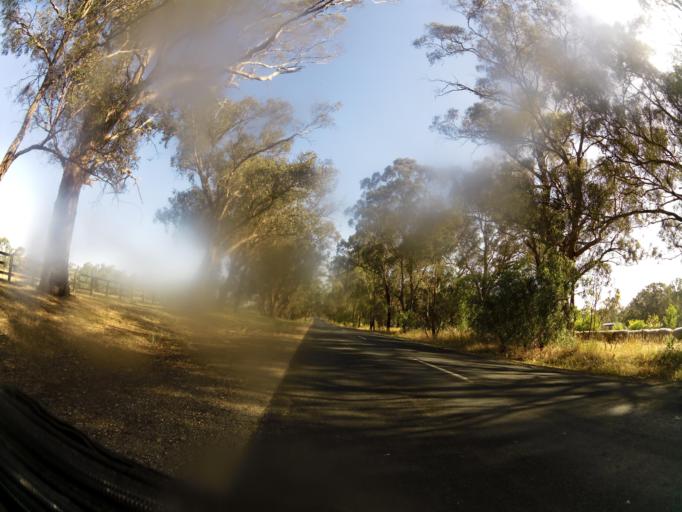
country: AU
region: Victoria
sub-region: Murrindindi
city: Kinglake West
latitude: -36.9592
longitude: 145.1076
